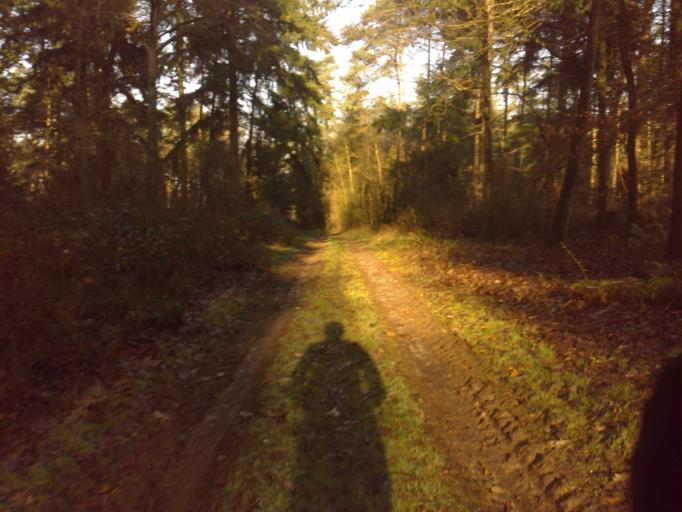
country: NL
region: Utrecht
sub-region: Gemeente Soest
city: Soest
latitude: 52.1430
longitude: 5.2743
